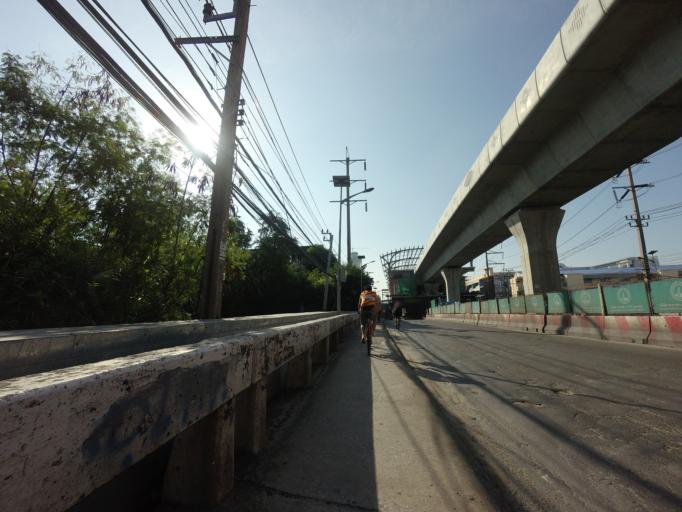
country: TH
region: Samut Prakan
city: Samut Prakan
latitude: 13.6035
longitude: 100.5968
